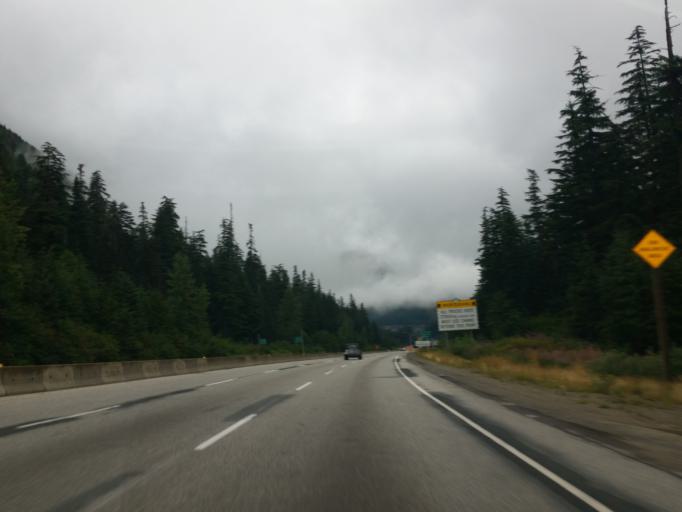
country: CA
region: British Columbia
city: Hope
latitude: 49.5737
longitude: -121.1815
